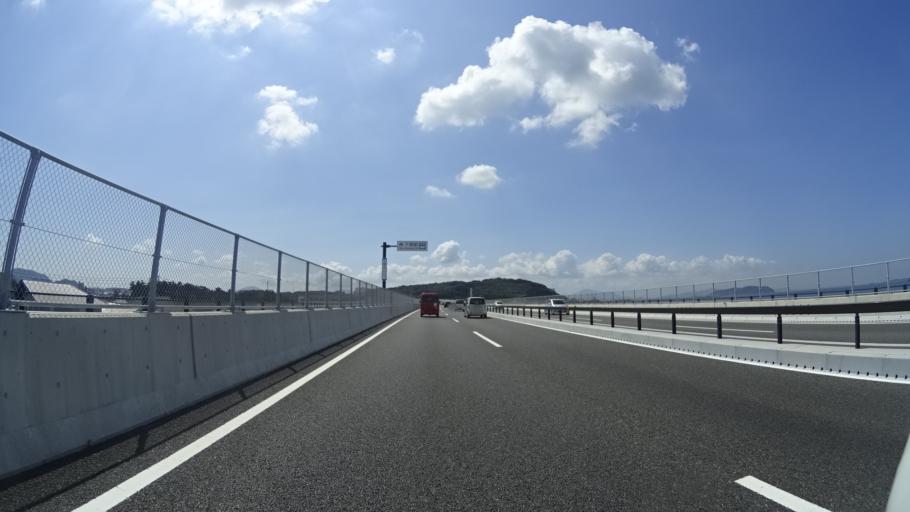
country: JP
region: Yamaguchi
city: Shimonoseki
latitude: 34.0094
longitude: 130.9164
